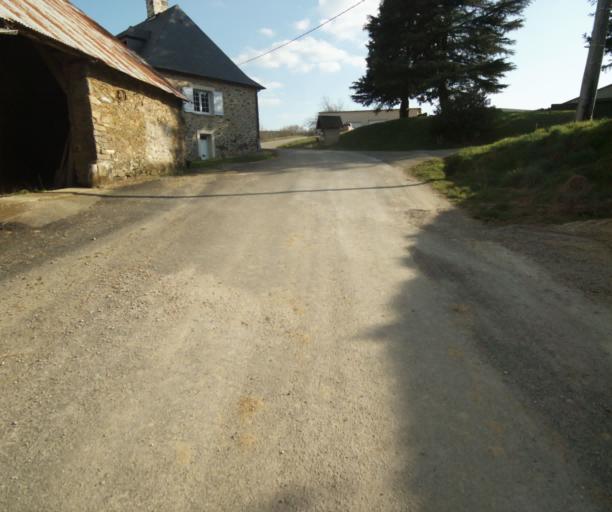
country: FR
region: Limousin
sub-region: Departement de la Correze
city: Saint-Mexant
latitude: 45.3451
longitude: 1.6098
